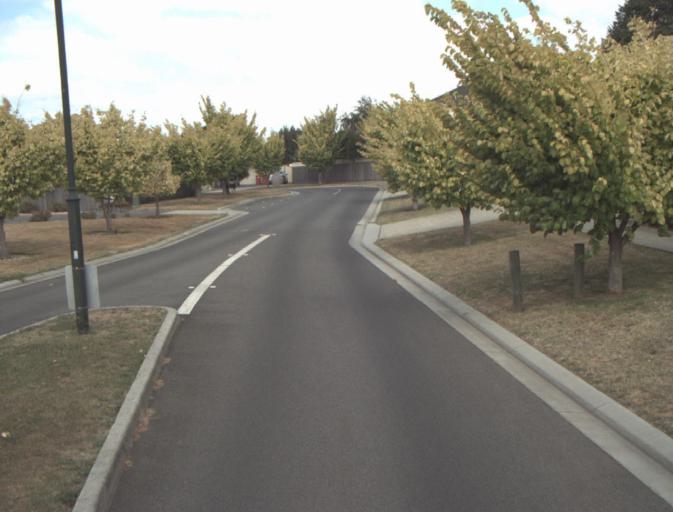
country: AU
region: Tasmania
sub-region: Launceston
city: East Launceston
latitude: -41.4328
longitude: 147.1566
